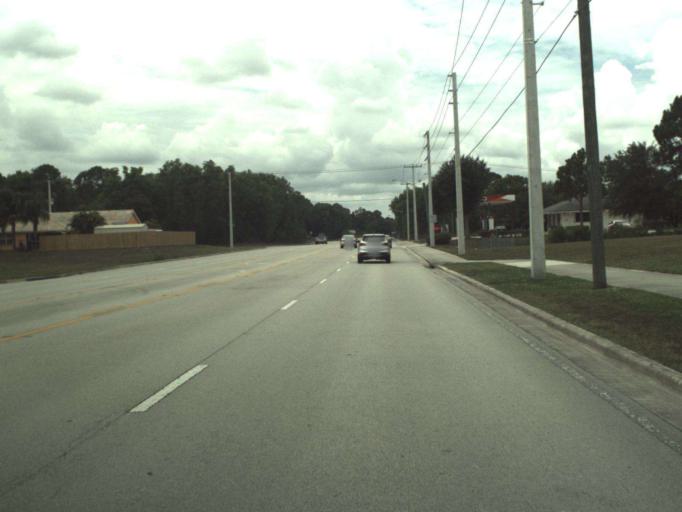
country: US
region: Florida
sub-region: Saint Lucie County
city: River Park
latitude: 27.3385
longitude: -80.3505
